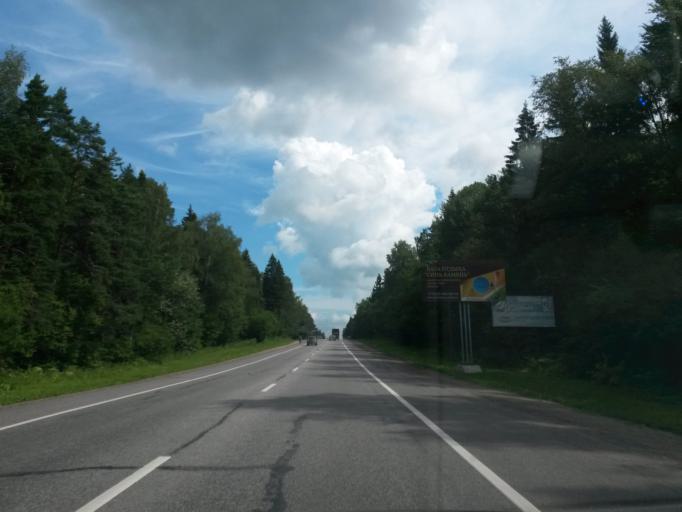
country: RU
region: Jaroslavl
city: Pereslavl'-Zalesskiy
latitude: 56.6951
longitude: 38.7666
